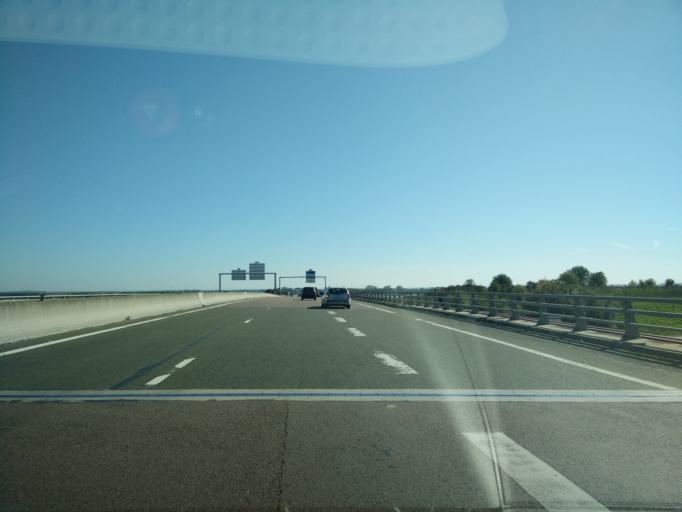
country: FR
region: Ile-de-France
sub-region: Departement de Seine-et-Marne
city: Mitry-Mory
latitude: 49.0031
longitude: 2.6296
